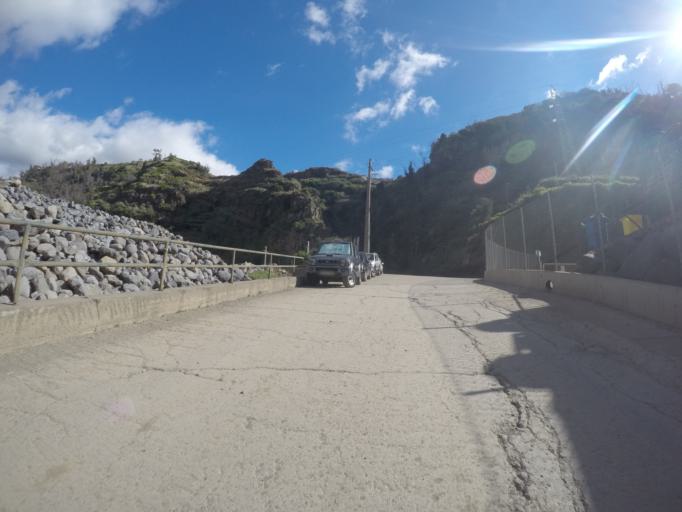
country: PT
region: Madeira
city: Camara de Lobos
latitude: 32.6611
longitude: -16.9612
